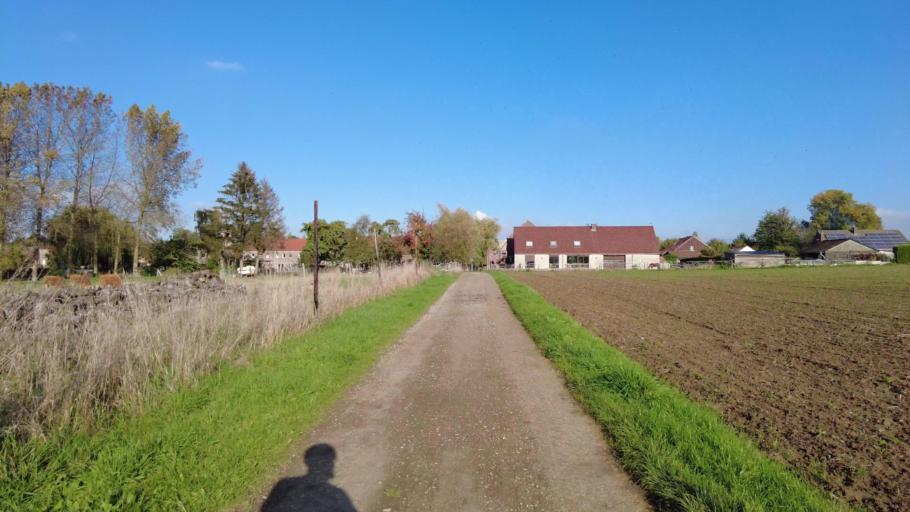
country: BE
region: Wallonia
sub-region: Province du Brabant Wallon
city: Jodoigne
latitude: 50.7365
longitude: 4.8931
